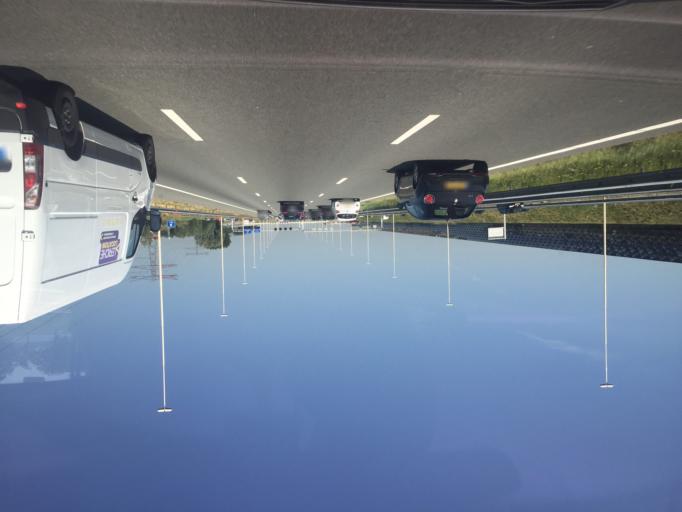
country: NL
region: Utrecht
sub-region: Stichtse Vecht
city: Maarssen
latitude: 52.1133
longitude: 5.0450
